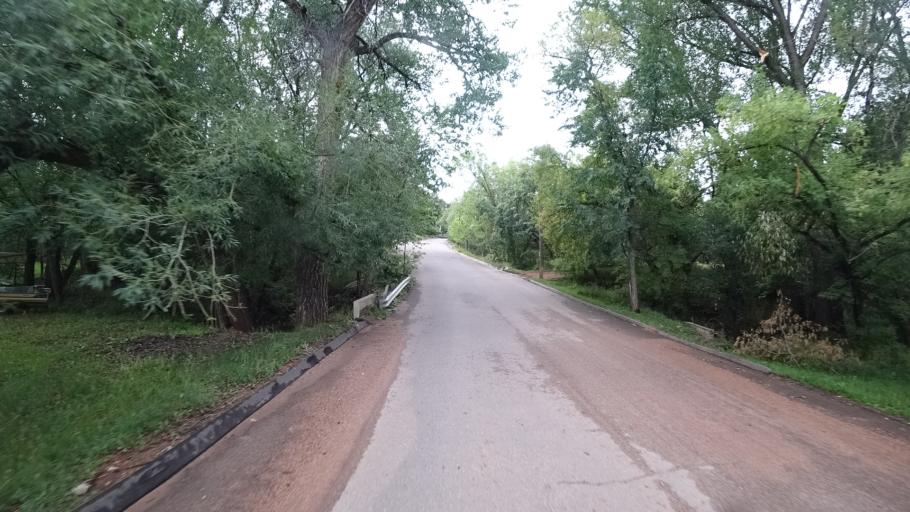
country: US
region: Colorado
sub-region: El Paso County
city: Manitou Springs
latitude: 38.8534
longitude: -104.8950
